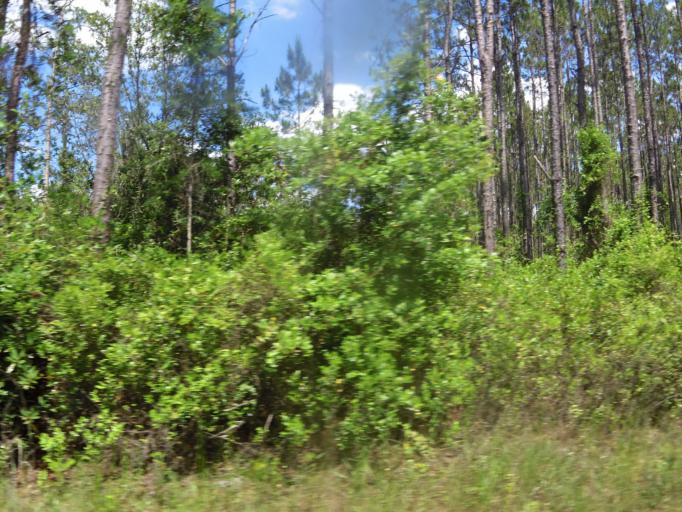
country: US
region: Florida
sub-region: Clay County
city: Asbury Lake
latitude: 29.8658
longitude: -81.8535
